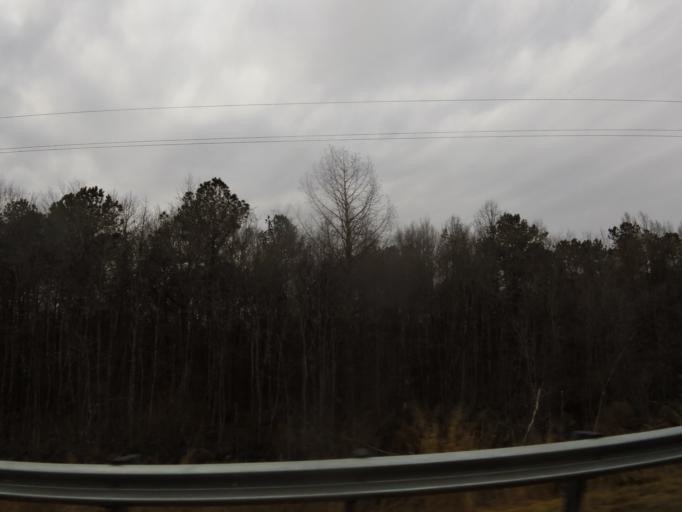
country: US
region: North Carolina
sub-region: Halifax County
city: Scotland Neck
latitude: 36.2404
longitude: -77.3459
